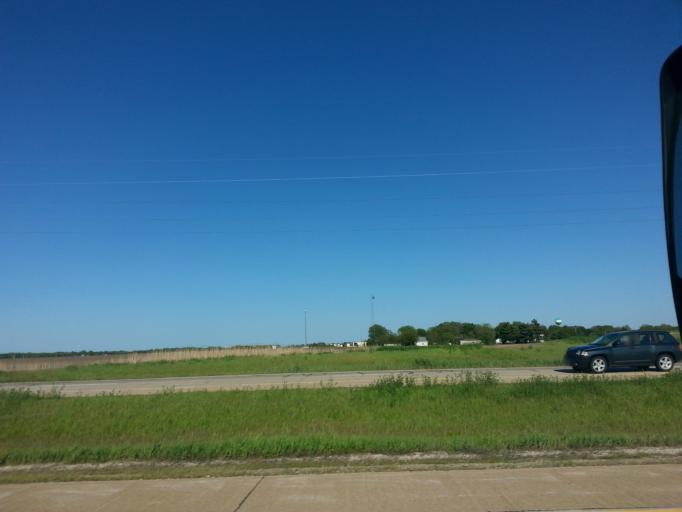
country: US
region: Illinois
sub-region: LaSalle County
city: Oglesby
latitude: 41.2231
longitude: -89.0780
